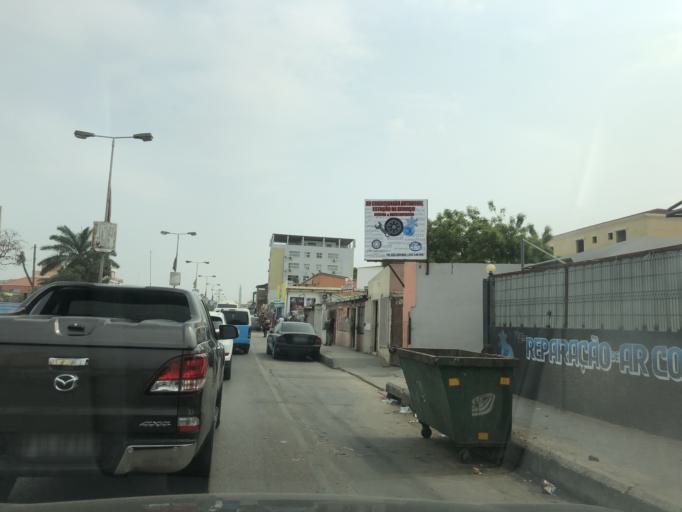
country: AO
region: Luanda
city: Luanda
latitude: -8.8418
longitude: 13.2133
